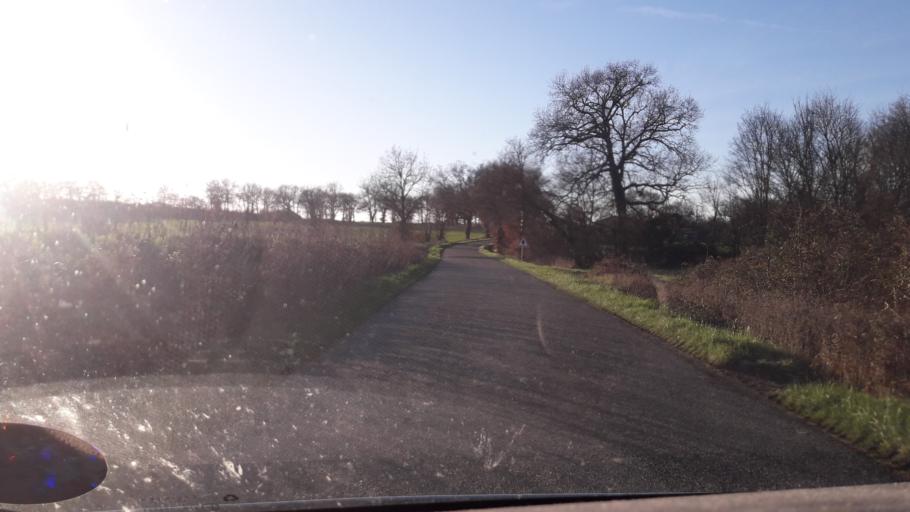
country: FR
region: Midi-Pyrenees
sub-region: Departement du Gers
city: Gimont
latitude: 43.6404
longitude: 0.9893
